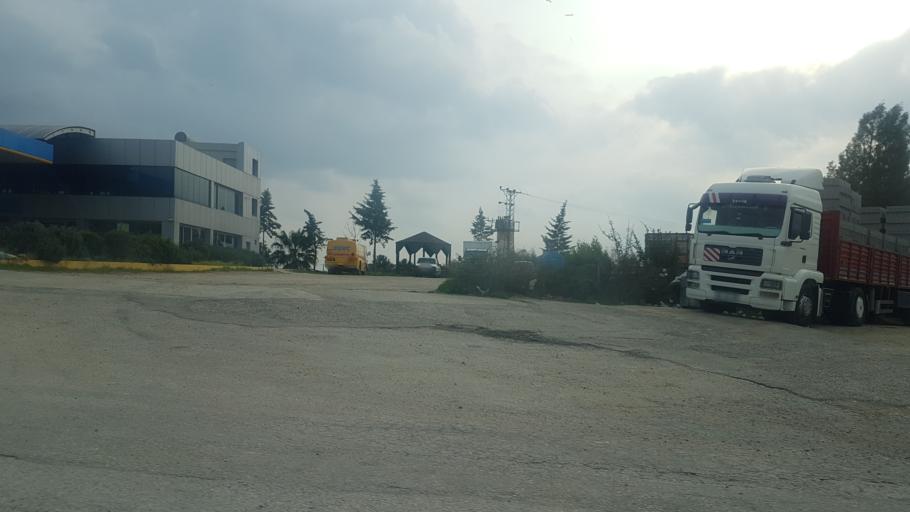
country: TR
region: Mersin
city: Yenice
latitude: 37.0544
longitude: 35.1701
